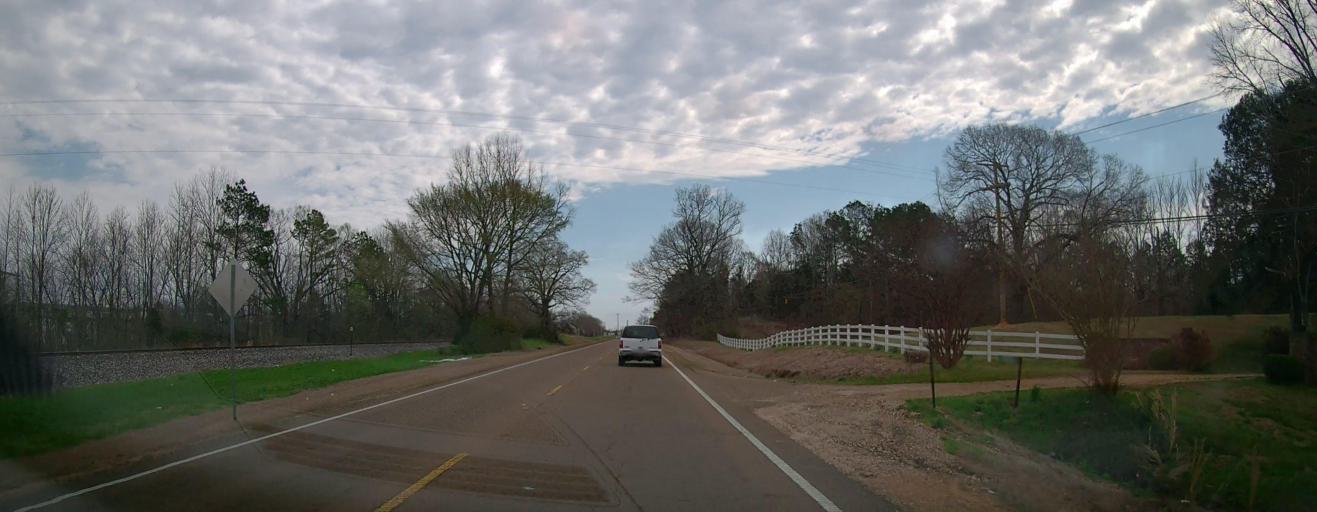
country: US
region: Mississippi
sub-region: Marshall County
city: Byhalia
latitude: 34.8698
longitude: -89.6741
